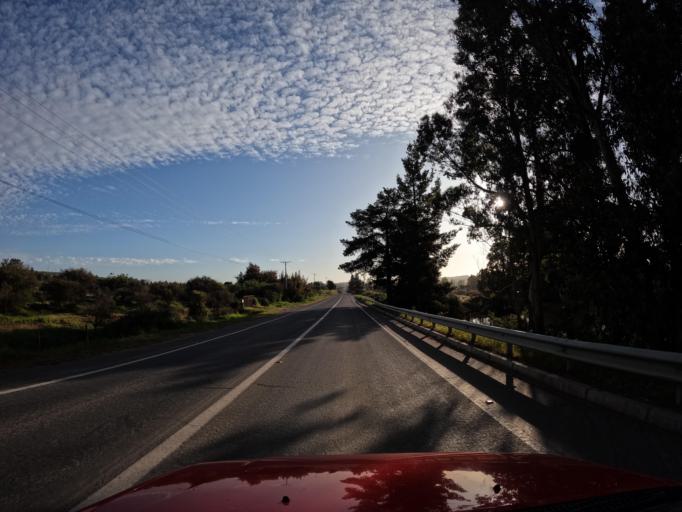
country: CL
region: Valparaiso
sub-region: San Antonio Province
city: San Antonio
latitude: -34.0978
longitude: -71.6936
